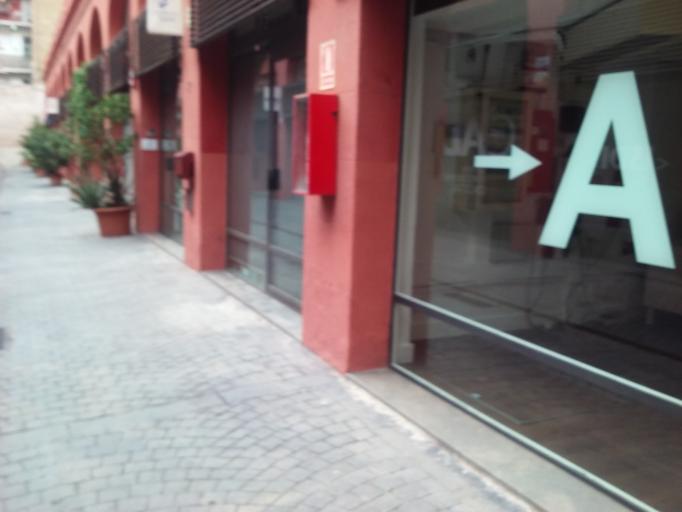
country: ES
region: Catalonia
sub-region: Provincia de Barcelona
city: Sants-Montjuic
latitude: 41.3793
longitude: 2.1517
